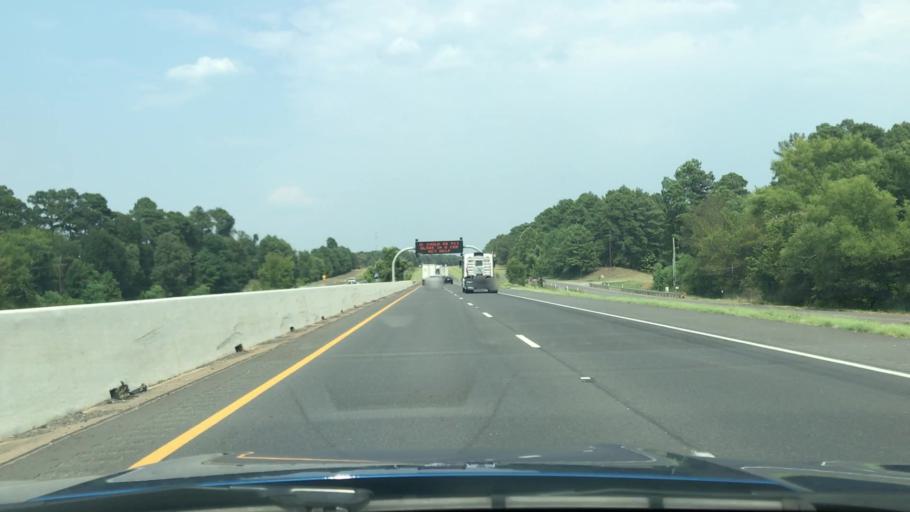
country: US
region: Texas
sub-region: Gregg County
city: Longview
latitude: 32.4529
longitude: -94.7009
